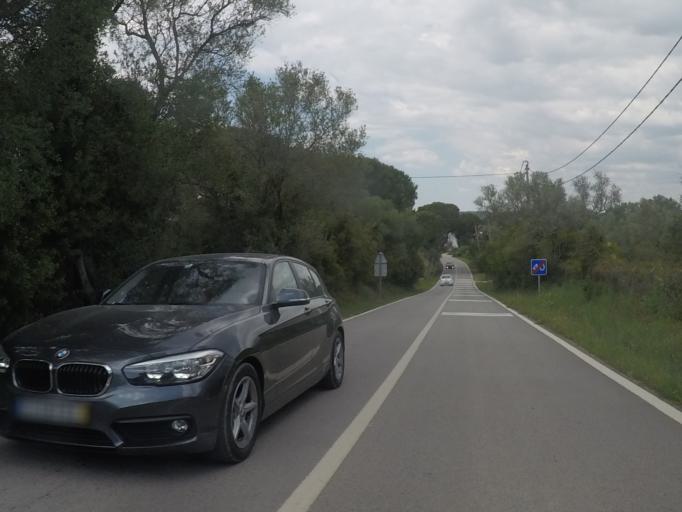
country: PT
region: Setubal
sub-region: Sesimbra
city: Sesimbra
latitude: 38.4715
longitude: -9.0302
